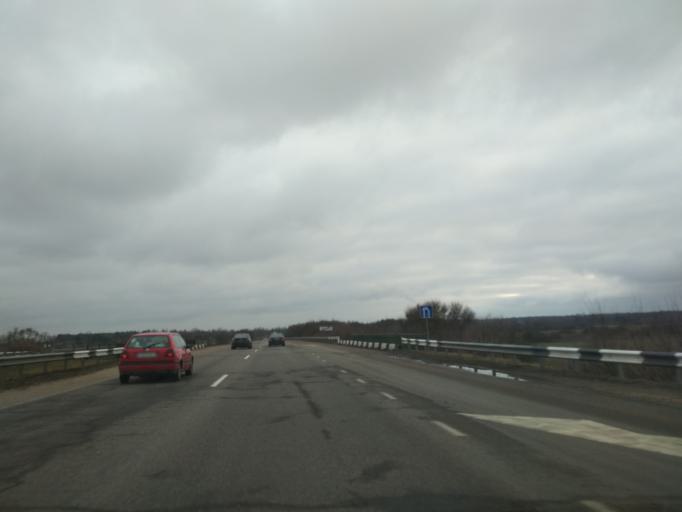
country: BY
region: Minsk
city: Dukora
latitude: 53.6679
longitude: 27.9367
